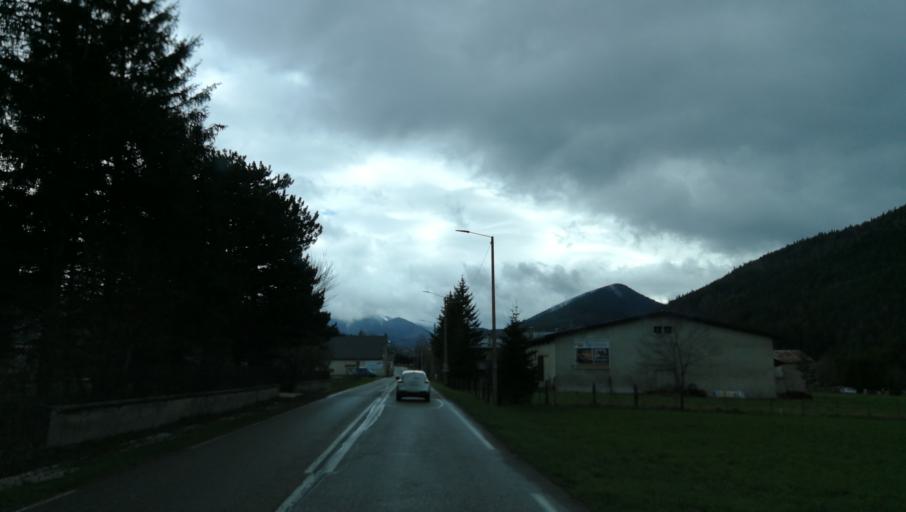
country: FR
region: Rhone-Alpes
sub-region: Departement de l'Isere
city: Villard-de-Lans
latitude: 45.0877
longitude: 5.5549
